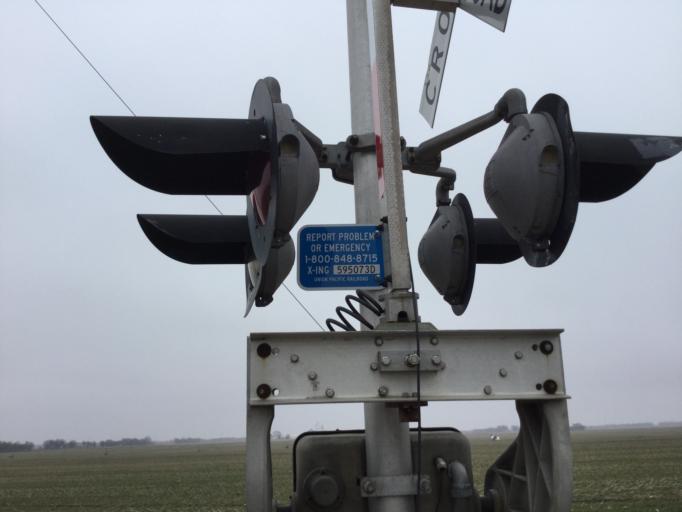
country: US
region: Kansas
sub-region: Sedgwick County
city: Haysville
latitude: 37.4963
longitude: -97.3693
